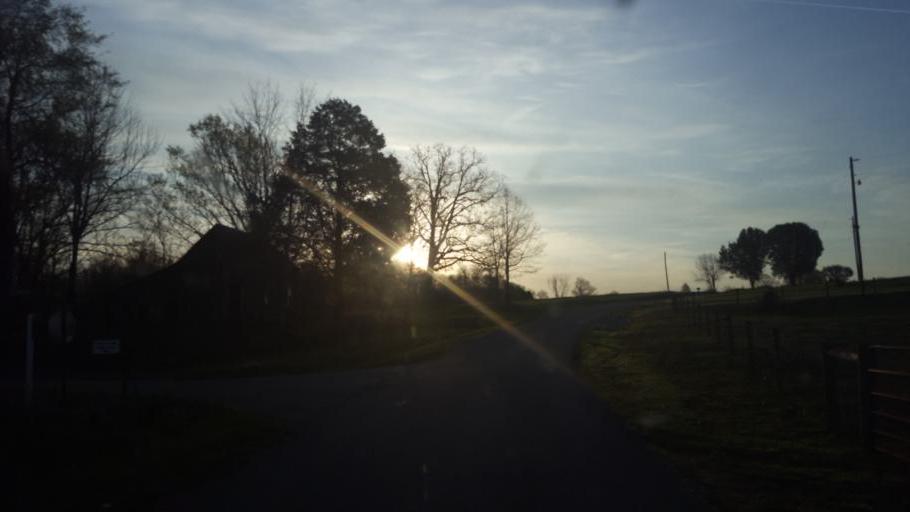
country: US
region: Kentucky
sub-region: Barren County
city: Cave City
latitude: 37.1750
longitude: -85.9981
